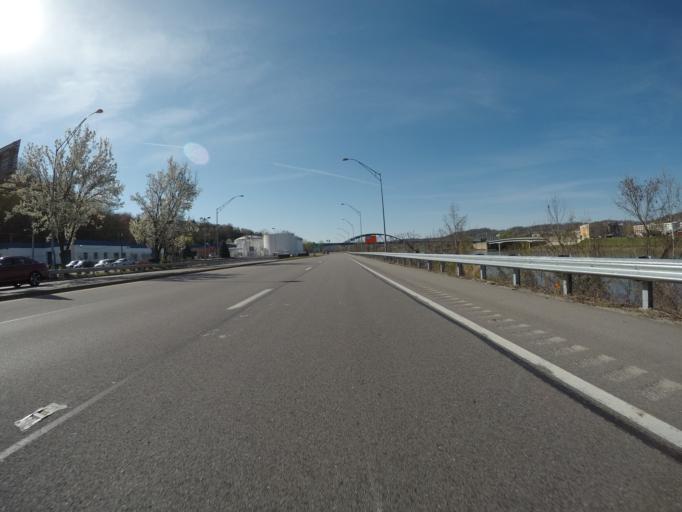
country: US
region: West Virginia
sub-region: Kanawha County
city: Charleston
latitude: 38.3509
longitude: -81.6437
